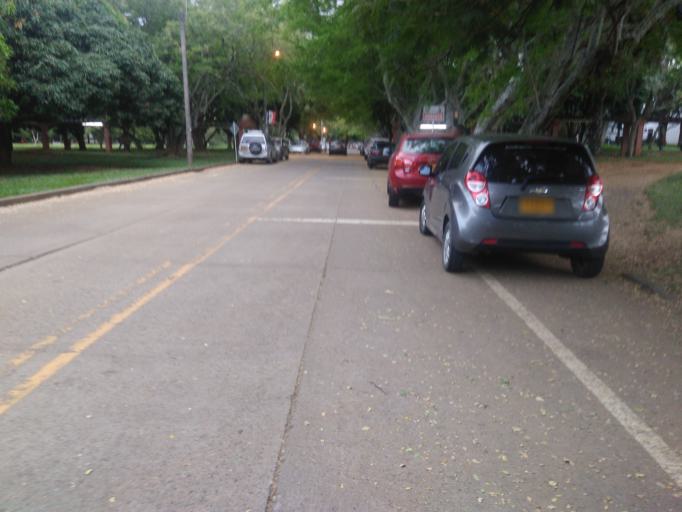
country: CO
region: Valle del Cauca
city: Cali
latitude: 3.3755
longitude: -76.5364
